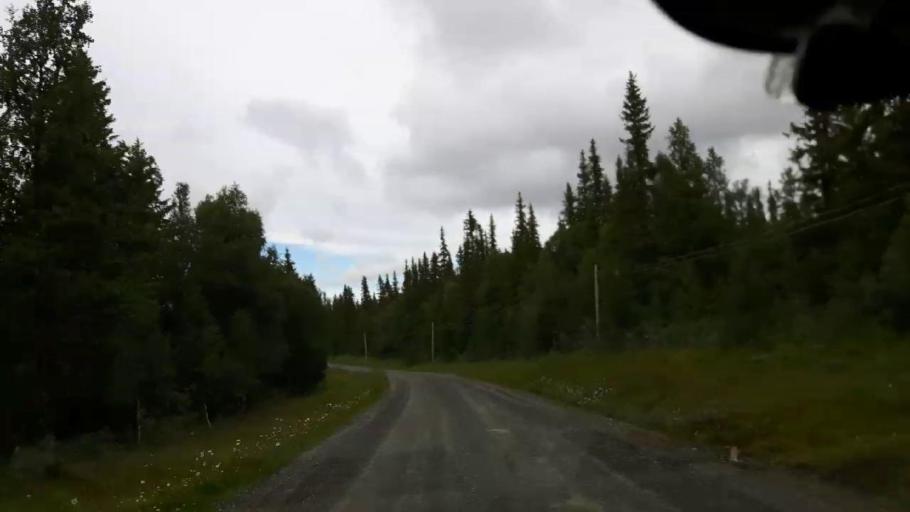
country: SE
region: Jaemtland
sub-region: Krokoms Kommun
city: Valla
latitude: 63.7641
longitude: 13.8370
